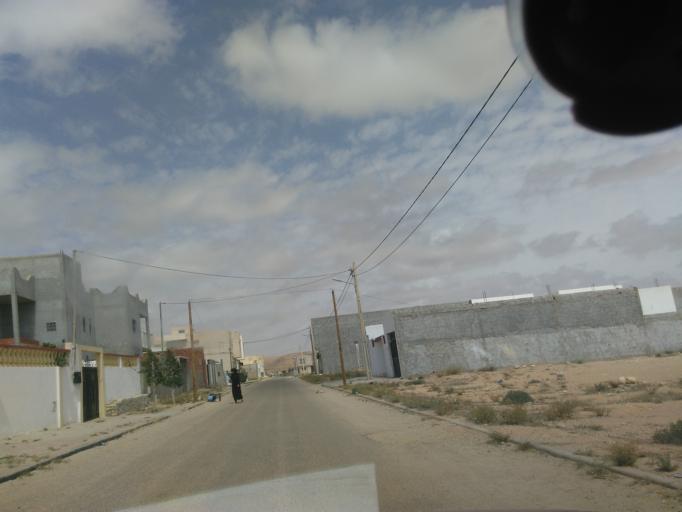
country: TN
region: Tataouine
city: Tataouine
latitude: 32.9536
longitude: 10.4672
